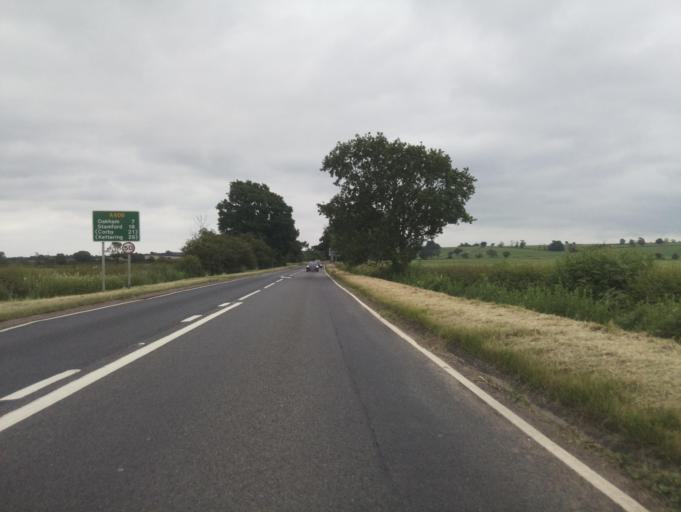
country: GB
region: England
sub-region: Leicestershire
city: Melton Mowbray
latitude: 52.7281
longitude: -0.8441
